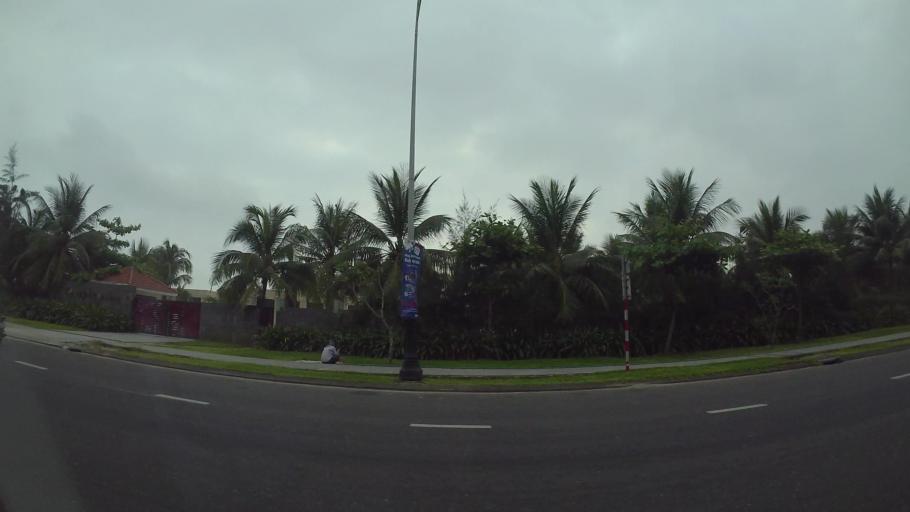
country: VN
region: Da Nang
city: Son Tra
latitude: 16.0751
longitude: 108.2452
